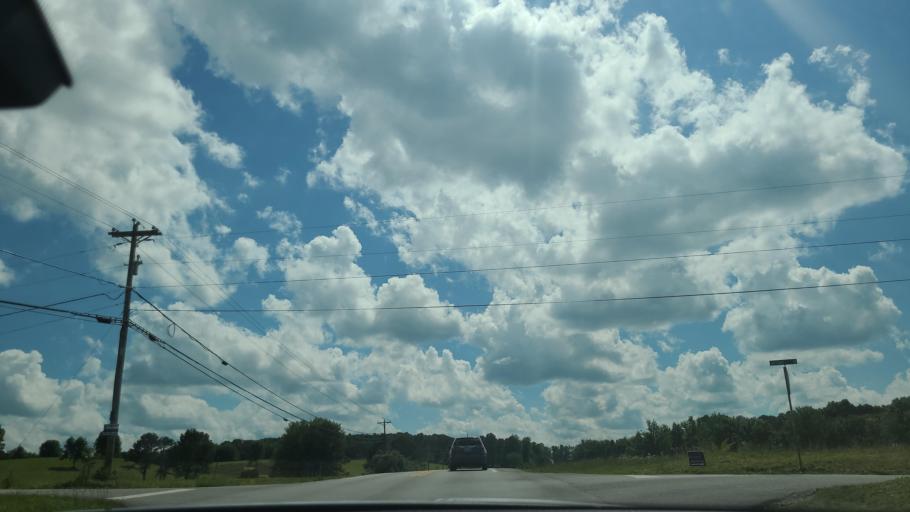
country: US
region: Kentucky
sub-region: Whitley County
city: Corbin
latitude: 36.9007
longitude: -84.1731
